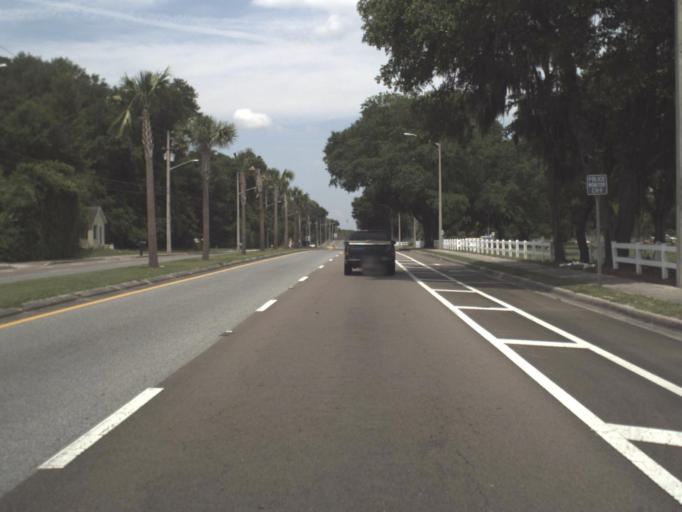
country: US
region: Florida
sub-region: Alachua County
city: Gainesville
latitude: 29.6376
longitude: -82.2774
